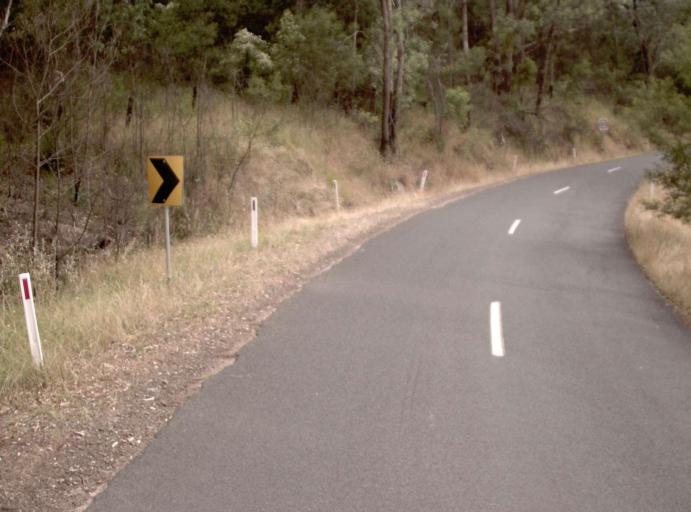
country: AU
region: Victoria
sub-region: Wellington
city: Heyfield
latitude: -37.7443
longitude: 146.6657
